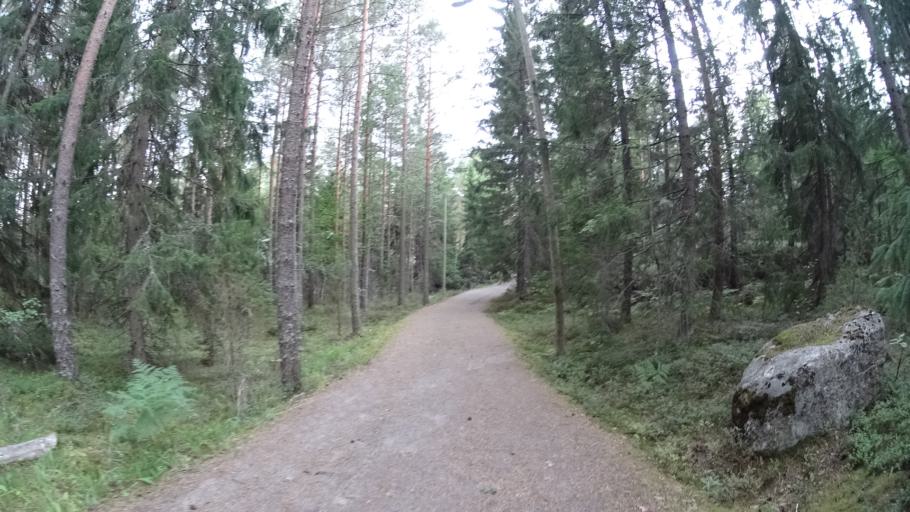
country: FI
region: Uusimaa
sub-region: Helsinki
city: Espoo
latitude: 60.2992
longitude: 24.5642
